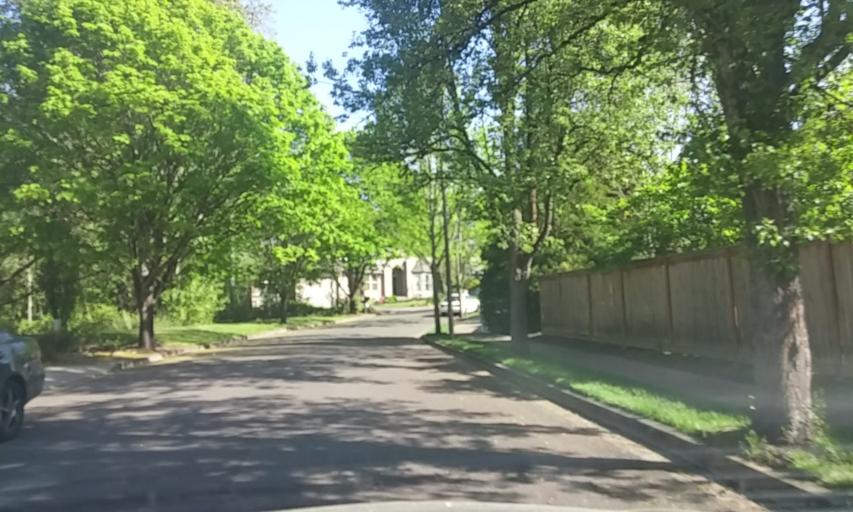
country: US
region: Oregon
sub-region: Washington County
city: Metzger
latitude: 45.4280
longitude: -122.7381
